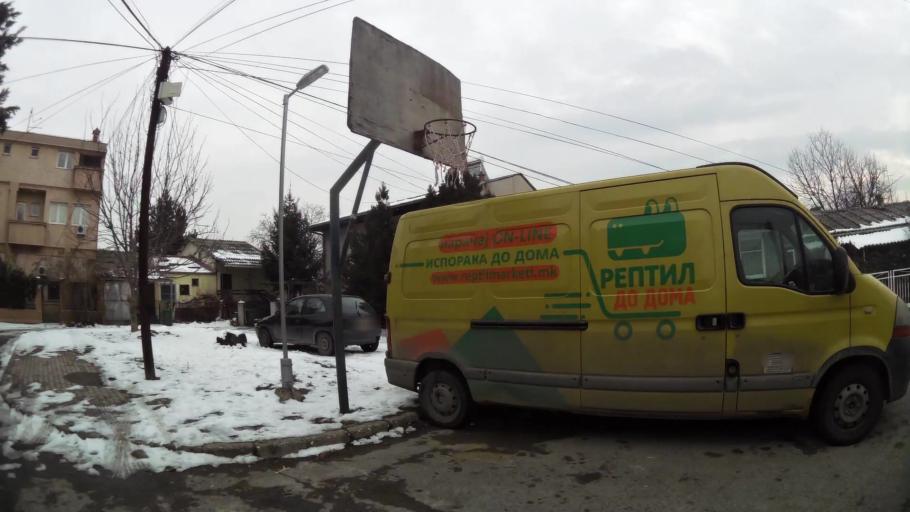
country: MK
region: Butel
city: Butel
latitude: 42.0342
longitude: 21.4451
